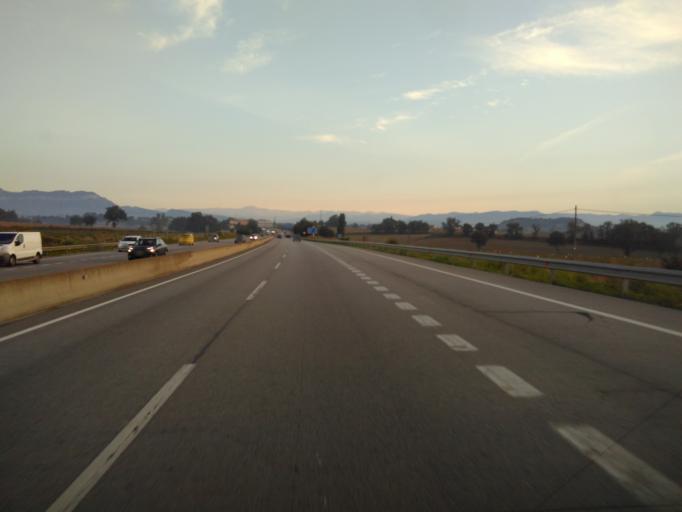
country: ES
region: Catalonia
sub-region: Provincia de Barcelona
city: Gurb
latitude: 41.9646
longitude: 2.2484
